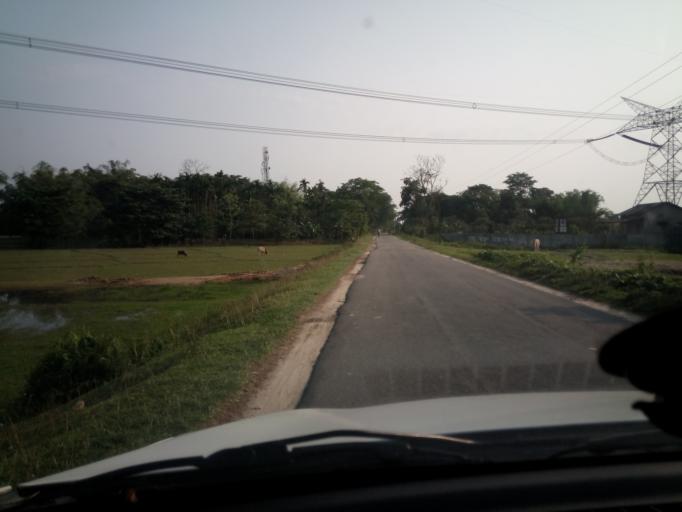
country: IN
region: Assam
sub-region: Udalguri
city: Udalguri
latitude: 26.7146
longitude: 92.0730
